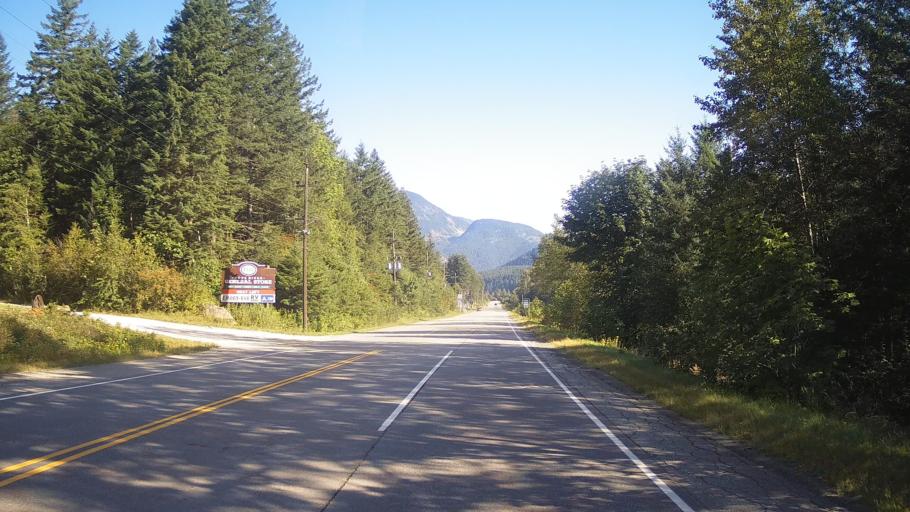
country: CA
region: British Columbia
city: Hope
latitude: 49.5156
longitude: -121.4198
